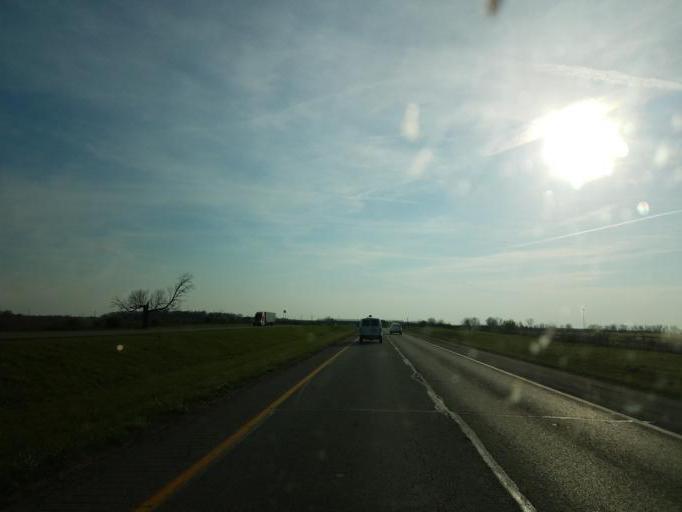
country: US
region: Ohio
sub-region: Clinton County
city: Wilmington
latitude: 39.4897
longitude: -83.9313
